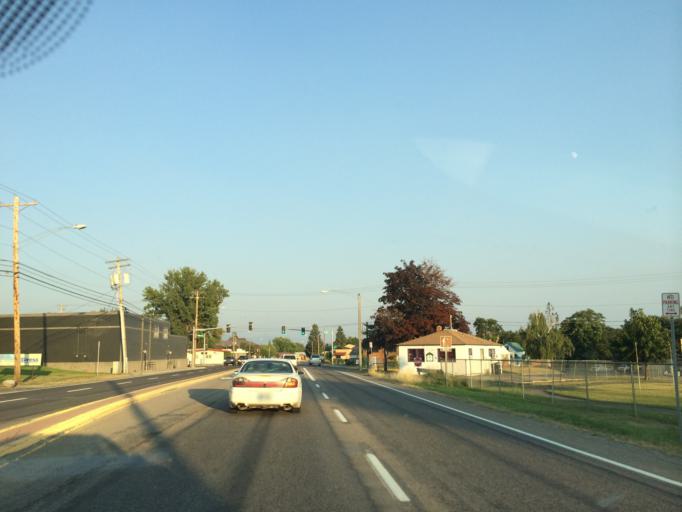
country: US
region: Montana
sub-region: Flathead County
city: Kalispell
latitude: 48.2071
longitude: -114.3207
